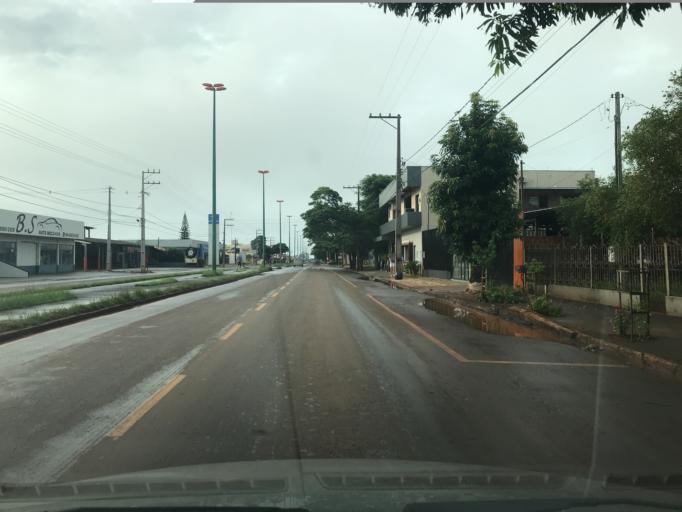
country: BR
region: Parana
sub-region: Palotina
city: Palotina
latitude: -24.3000
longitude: -53.8345
